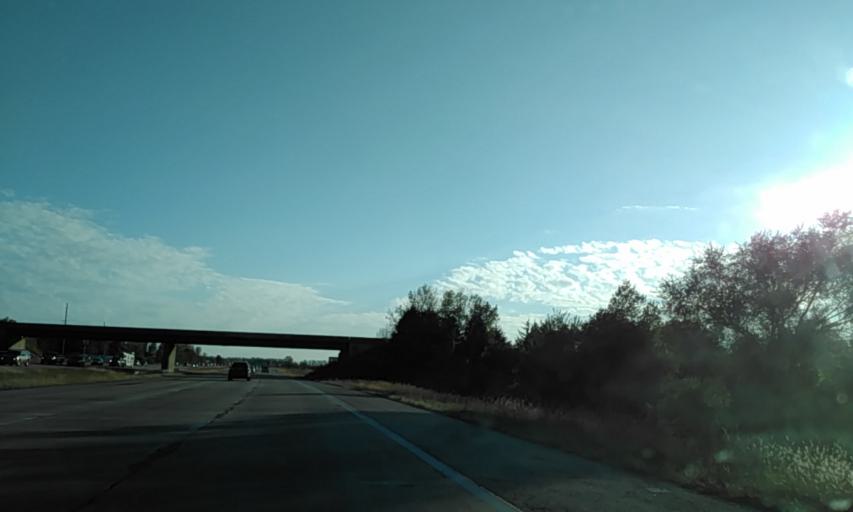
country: US
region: Illinois
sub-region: Saint Clair County
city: Dupo
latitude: 38.4914
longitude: -90.2177
